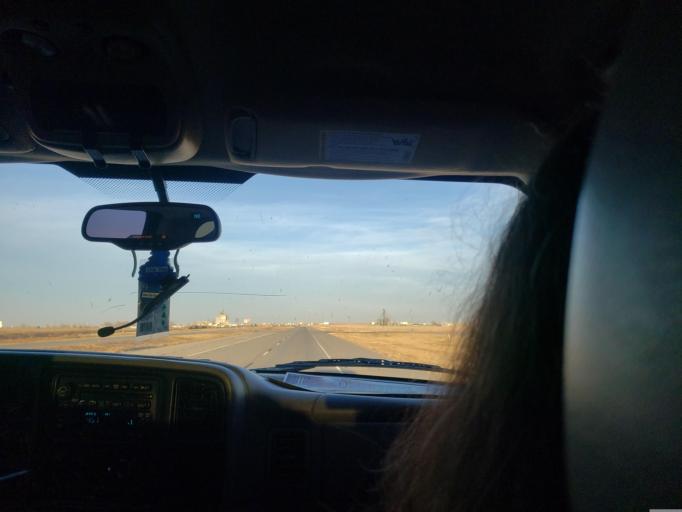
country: US
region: Oklahoma
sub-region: Texas County
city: Guymon
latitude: 36.7612
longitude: -101.3550
